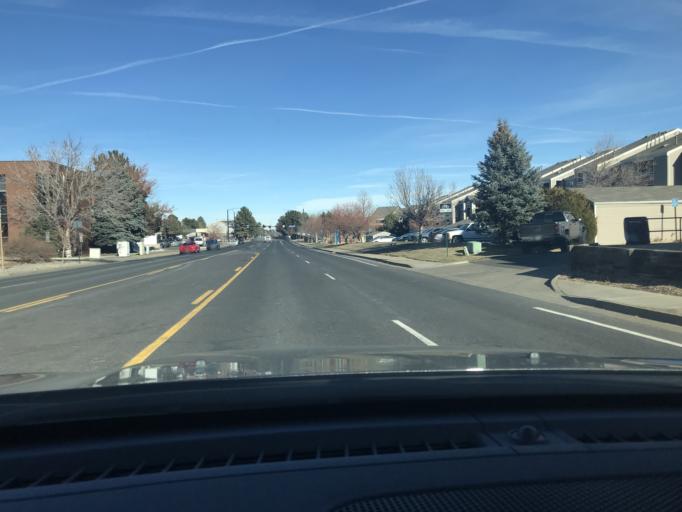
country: US
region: Colorado
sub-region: Arapahoe County
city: Centennial
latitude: 39.5966
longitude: -104.8762
